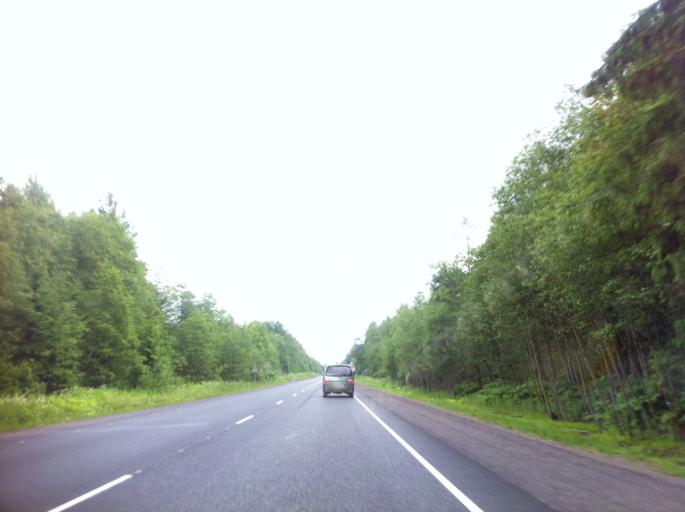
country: RU
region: Leningrad
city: Rozhdestveno
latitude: 59.1920
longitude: 29.9205
